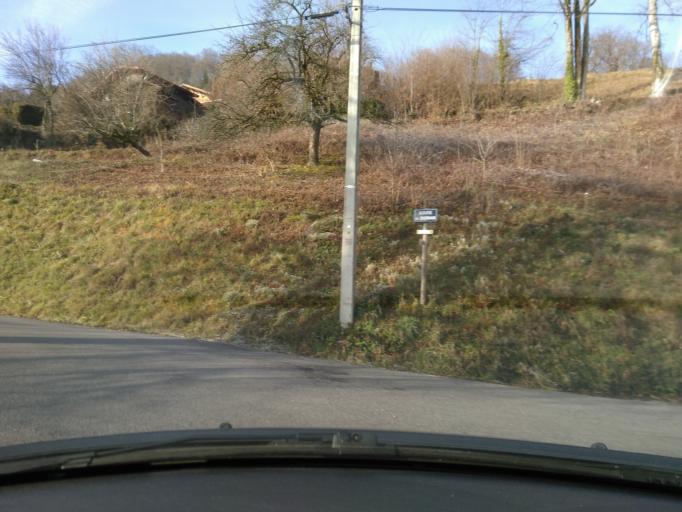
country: FR
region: Rhone-Alpes
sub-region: Departement de la Haute-Savoie
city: Sallanches
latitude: 45.9495
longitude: 6.6211
